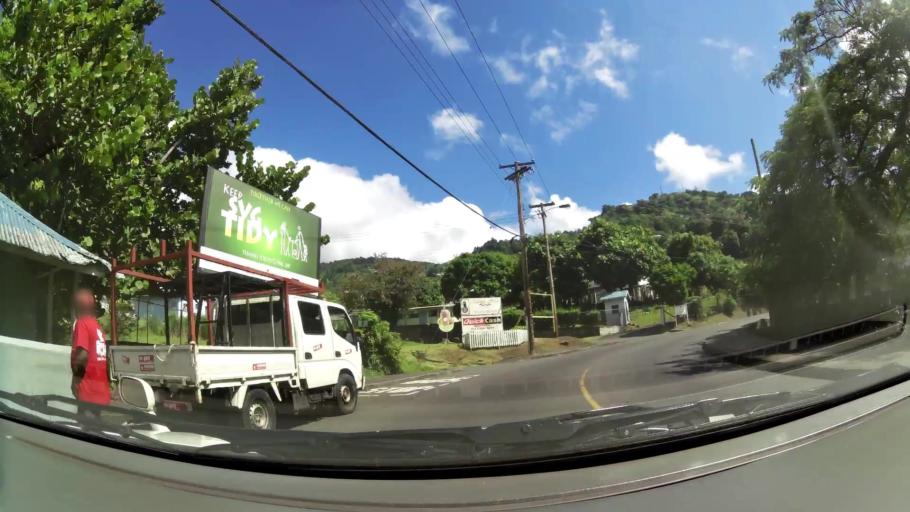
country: VC
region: Saint George
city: Kingstown
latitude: 13.1578
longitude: -61.2220
